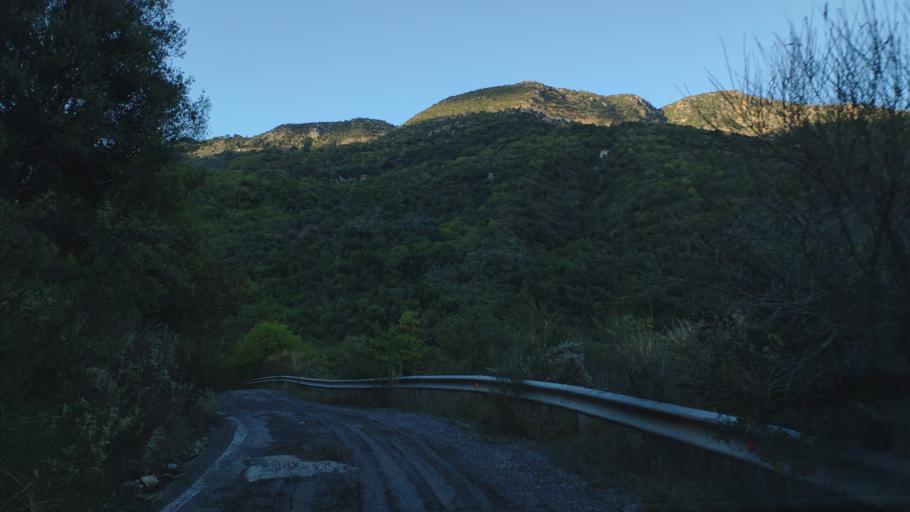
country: GR
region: Peloponnese
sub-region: Nomos Arkadias
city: Dimitsana
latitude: 37.5725
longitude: 22.0429
